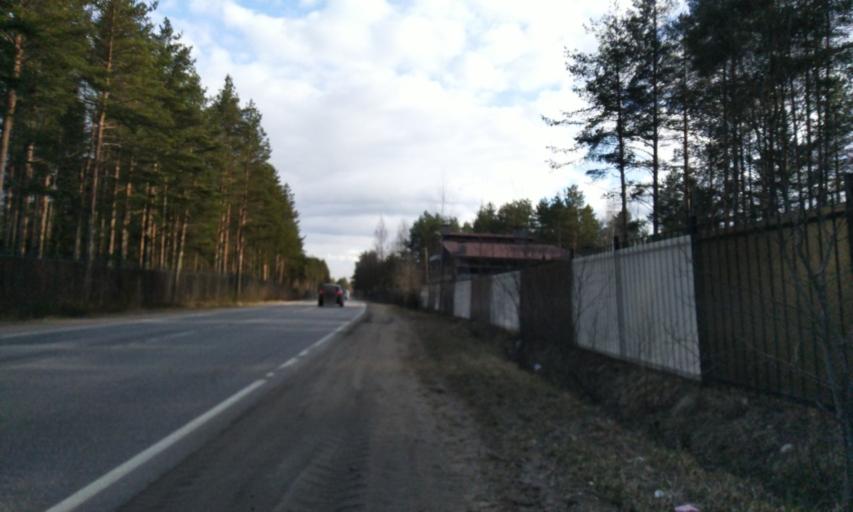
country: RU
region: Leningrad
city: Novoye Devyatkino
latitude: 60.1192
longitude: 30.4488
